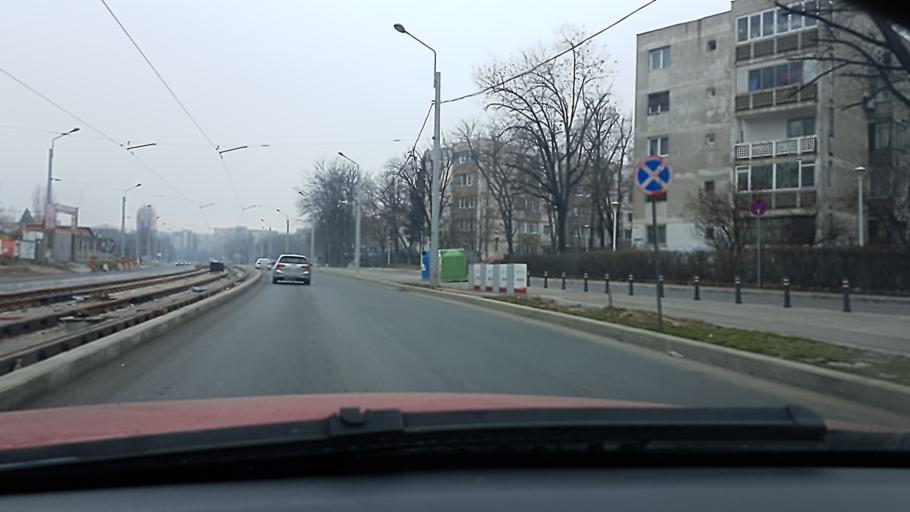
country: RO
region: Ilfov
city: Dobroesti
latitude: 44.4241
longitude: 26.1751
